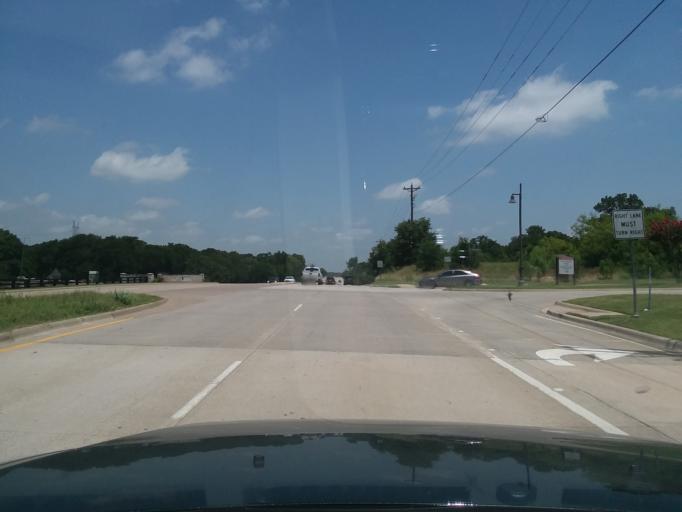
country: US
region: Texas
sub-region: Denton County
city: Bartonville
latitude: 33.0857
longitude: -97.1311
